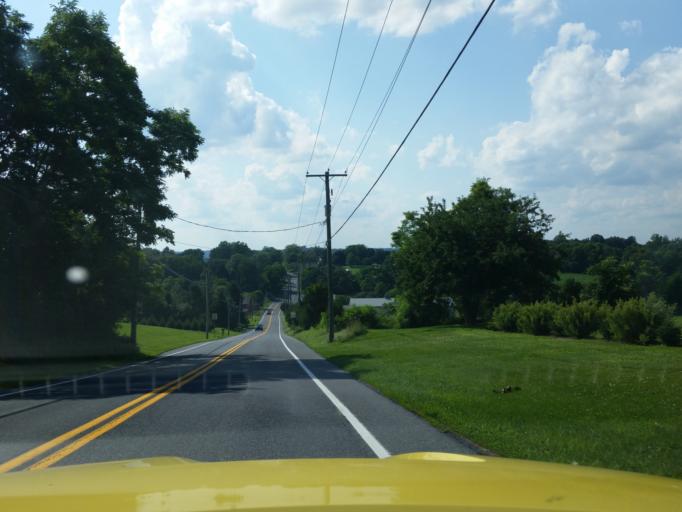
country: US
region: Pennsylvania
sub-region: Lancaster County
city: Manheim
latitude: 40.1843
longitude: -76.4665
